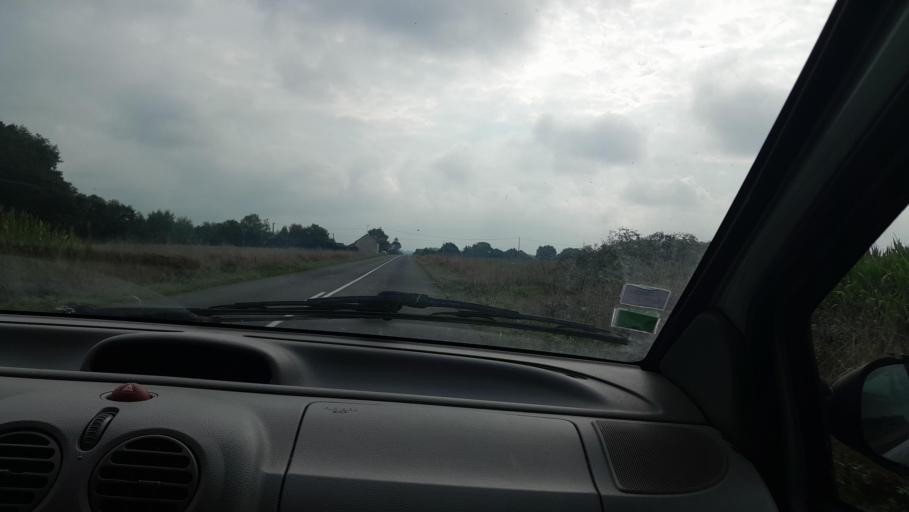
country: FR
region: Pays de la Loire
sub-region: Departement de la Mayenne
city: Cosse-le-Vivien
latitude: 47.9555
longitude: -0.9549
